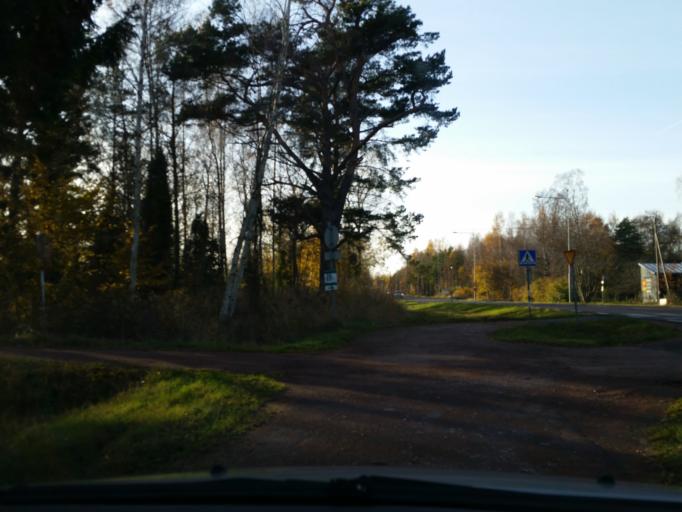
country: AX
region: Mariehamns stad
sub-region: Mariehamn
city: Mariehamn
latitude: 60.1161
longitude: 19.9649
